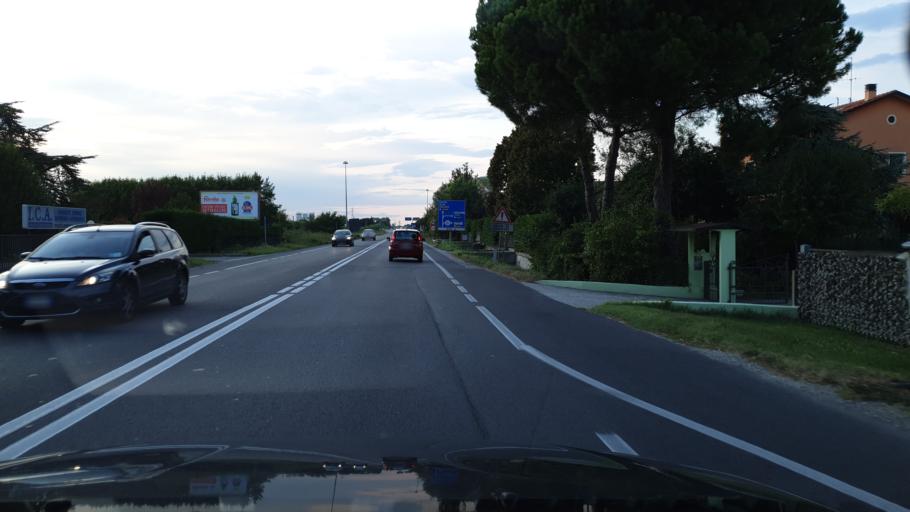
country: IT
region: Emilia-Romagna
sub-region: Forli-Cesena
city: Cesenatico
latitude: 44.1897
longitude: 12.4035
